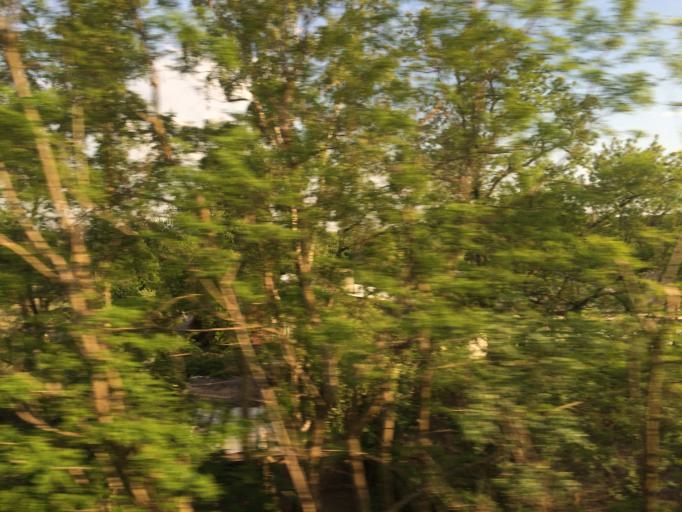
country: DE
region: North Rhine-Westphalia
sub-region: Regierungsbezirk Dusseldorf
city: Duisburg
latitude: 51.4453
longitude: 6.8060
